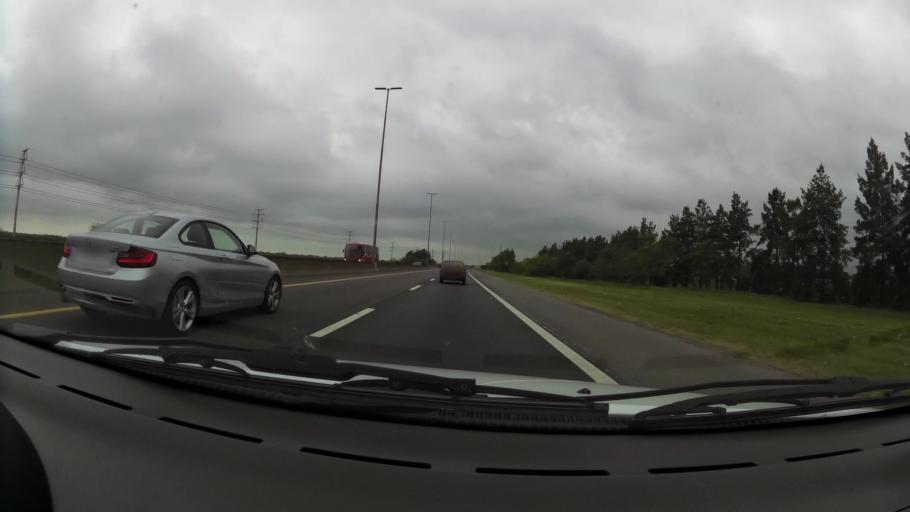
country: AR
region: Buenos Aires
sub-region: Partido de Quilmes
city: Quilmes
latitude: -34.7949
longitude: -58.1339
